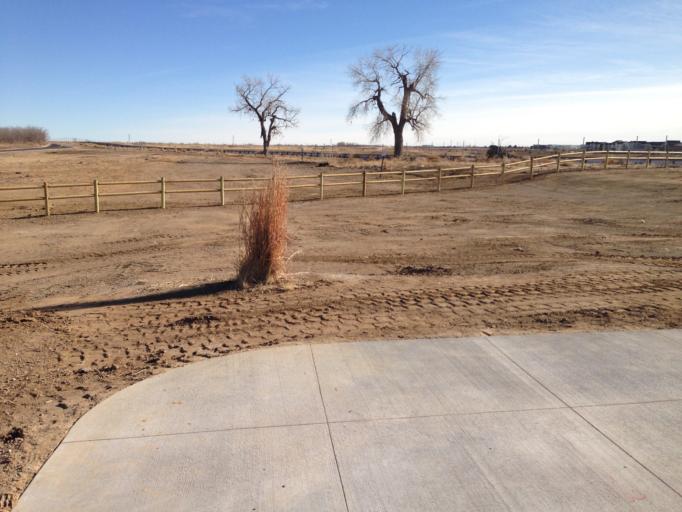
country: US
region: Colorado
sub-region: Adams County
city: Derby
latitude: 39.8133
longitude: -104.8843
